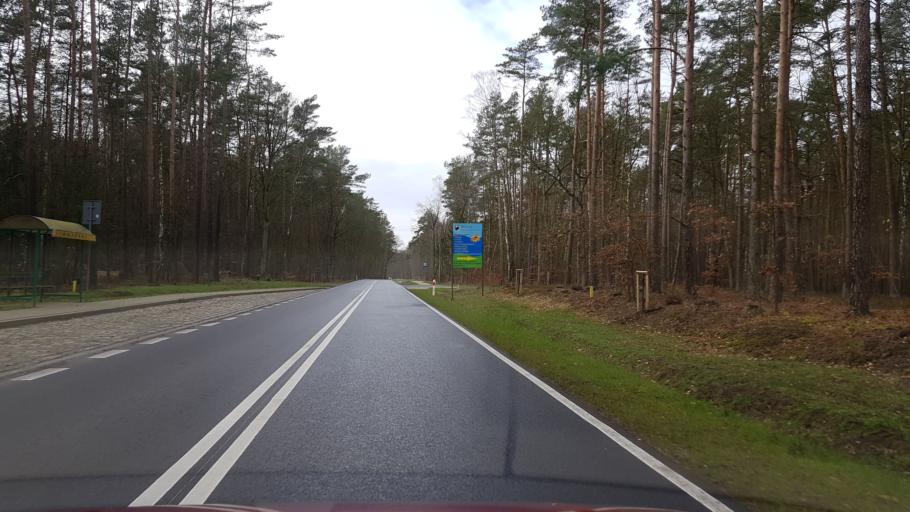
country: PL
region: West Pomeranian Voivodeship
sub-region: Powiat policki
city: Nowe Warpno
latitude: 53.6706
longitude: 14.4129
